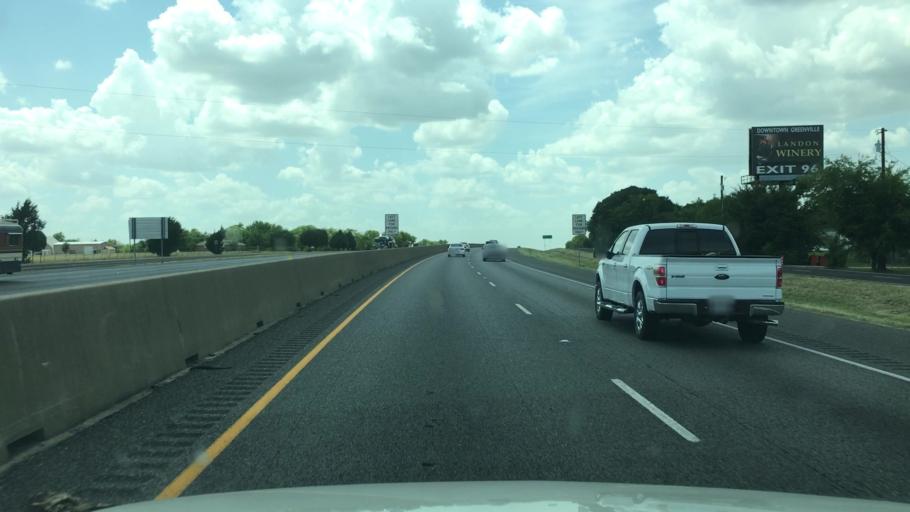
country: US
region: Texas
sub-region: Hunt County
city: Greenville
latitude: 33.1301
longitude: -96.0024
